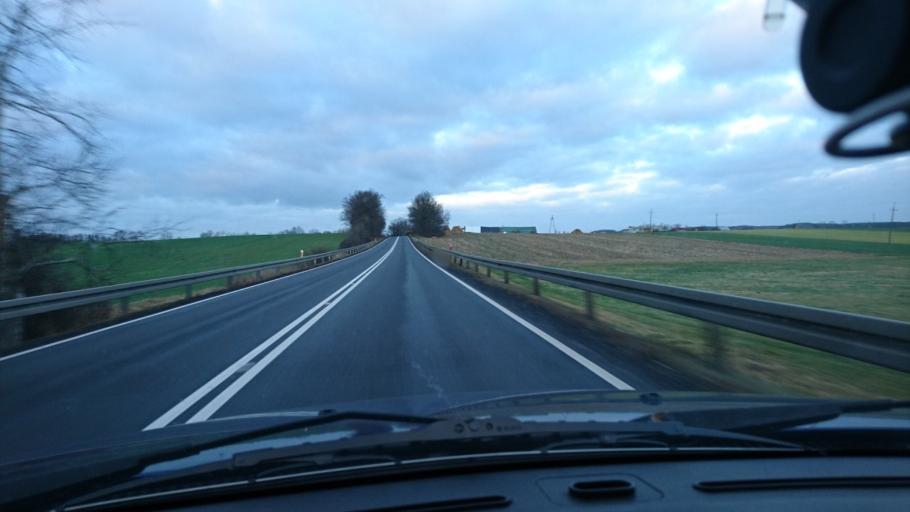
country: PL
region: Greater Poland Voivodeship
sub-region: Powiat ostrzeszowski
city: Ostrzeszow
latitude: 51.3765
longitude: 17.9435
